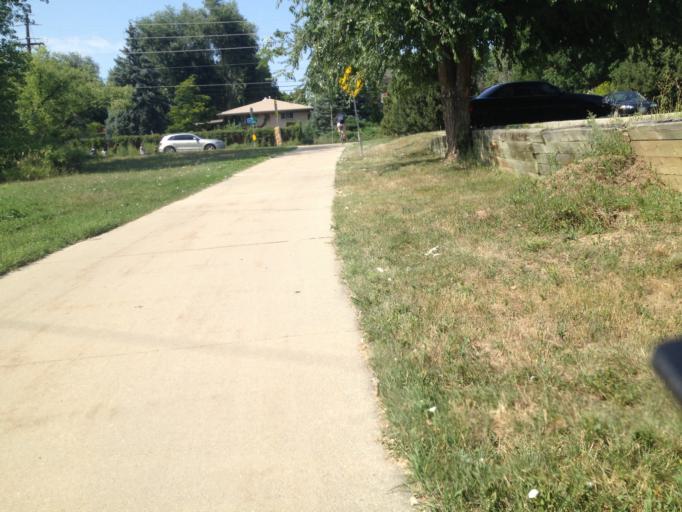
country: US
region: Colorado
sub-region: Boulder County
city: Boulder
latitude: 40.0287
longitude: -105.2652
